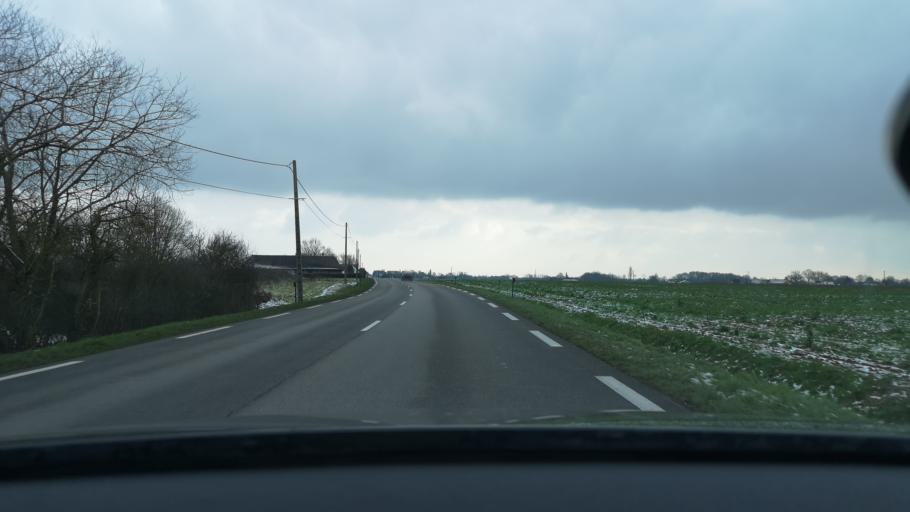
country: FR
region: Bourgogne
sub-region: Departement de Saone-et-Loire
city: Saint-Martin-en-Bresse
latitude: 46.7434
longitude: 5.0704
